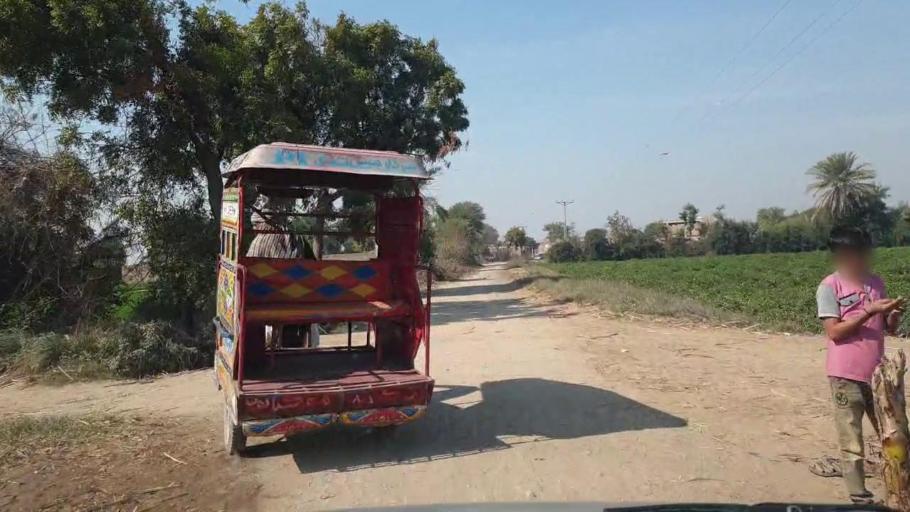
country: PK
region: Sindh
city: Tando Allahyar
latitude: 25.4137
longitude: 68.7529
